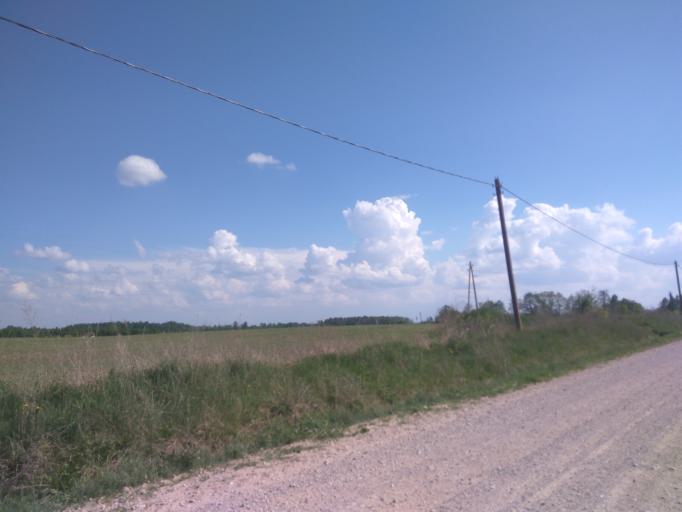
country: LV
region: Kuldigas Rajons
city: Kuldiga
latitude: 57.1628
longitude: 22.0187
